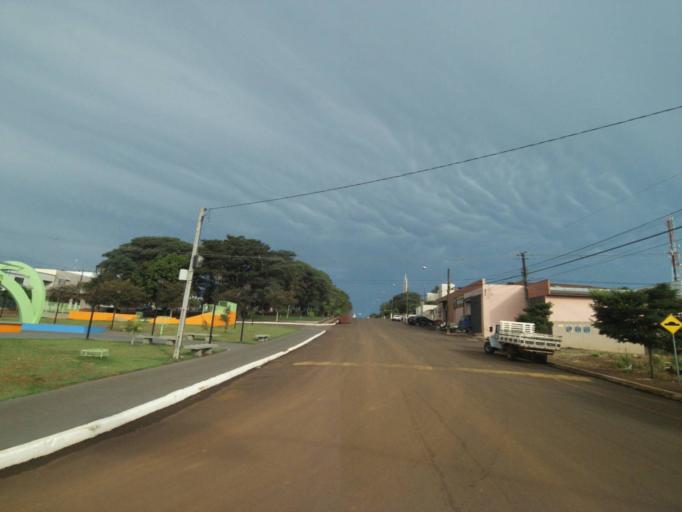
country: BR
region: Parana
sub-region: Guaraniacu
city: Guaraniacu
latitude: -25.1006
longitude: -52.8698
